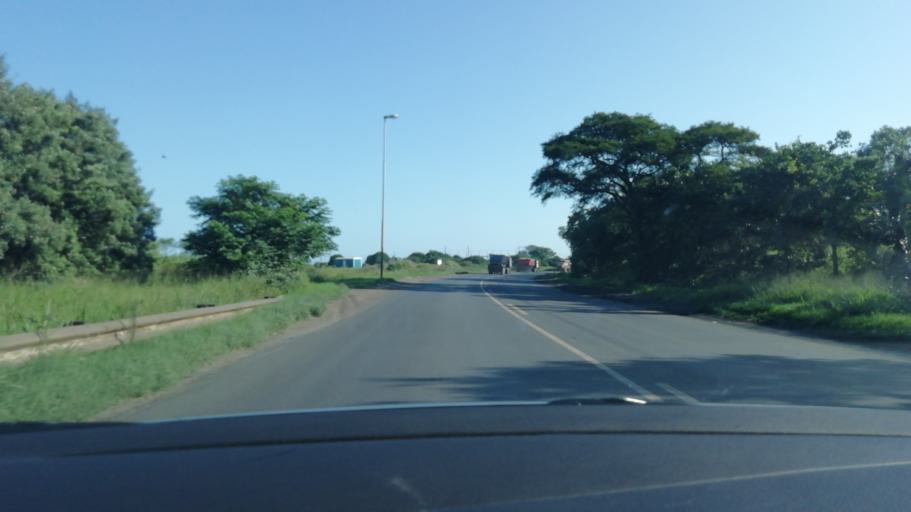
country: ZA
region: KwaZulu-Natal
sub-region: uThungulu District Municipality
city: Richards Bay
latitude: -28.7742
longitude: 32.0155
